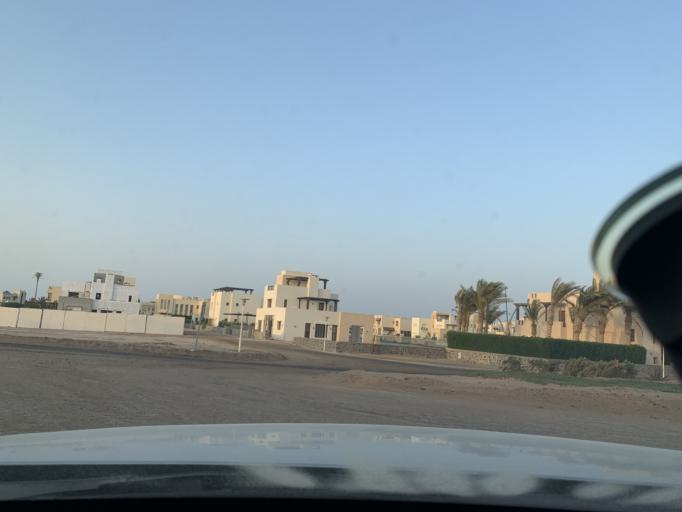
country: EG
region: Red Sea
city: El Gouna
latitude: 27.4119
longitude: 33.6678
